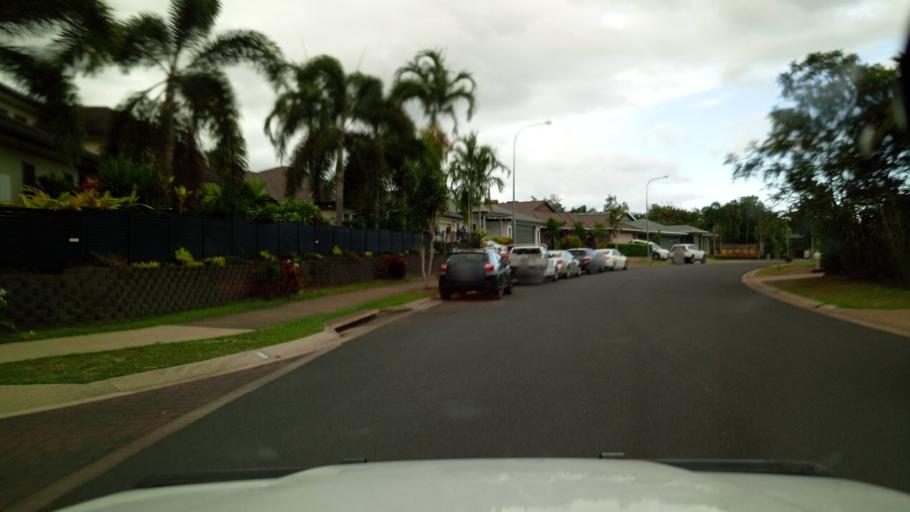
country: AU
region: Queensland
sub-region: Cairns
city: Redlynch
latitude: -16.8418
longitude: 145.6888
